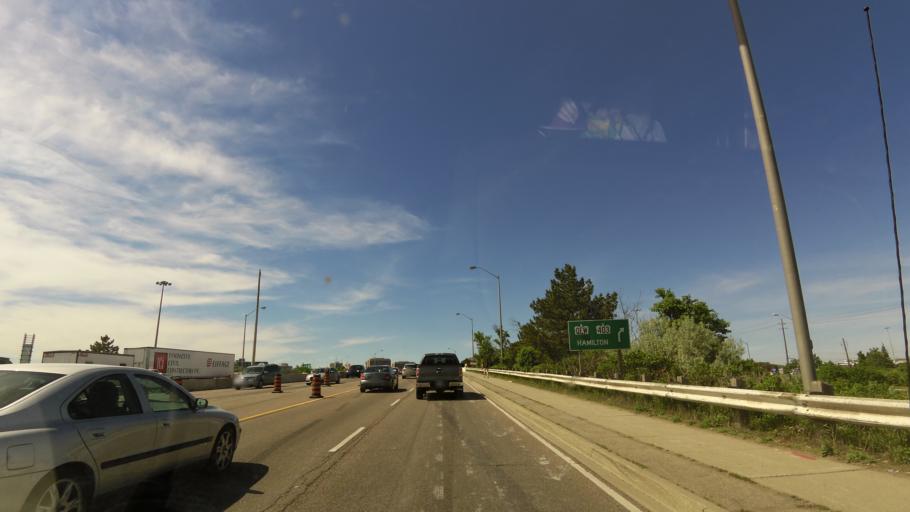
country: CA
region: Ontario
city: Oakville
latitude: 43.4602
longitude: -79.6829
